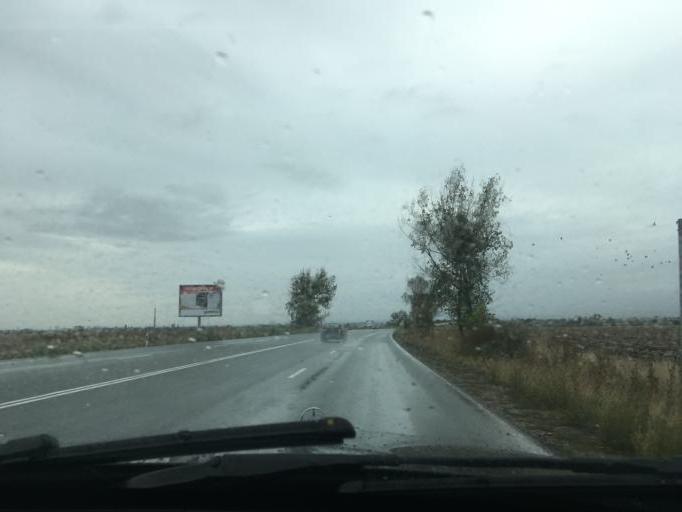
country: BG
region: Sofiya
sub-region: Obshtina Bozhurishte
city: Bozhurishte
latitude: 42.7637
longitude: 23.2161
